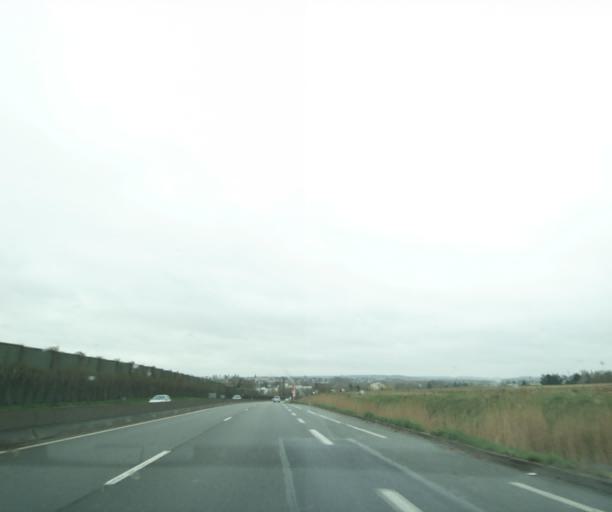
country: FR
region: Ile-de-France
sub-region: Departement de l'Essonne
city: Arpajon
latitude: 48.5952
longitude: 2.2431
